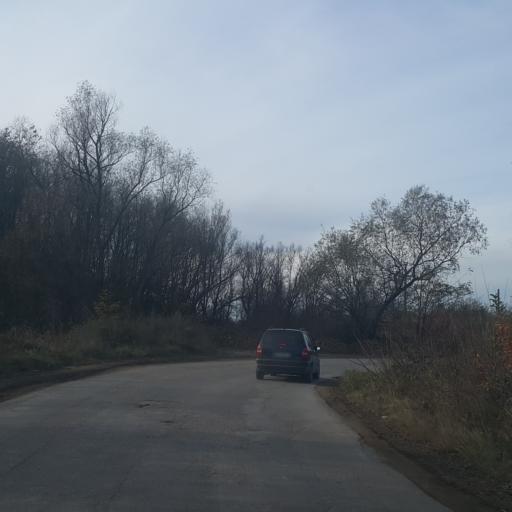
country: RS
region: Central Serbia
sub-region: Belgrade
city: Lazarevac
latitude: 44.4033
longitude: 20.3512
